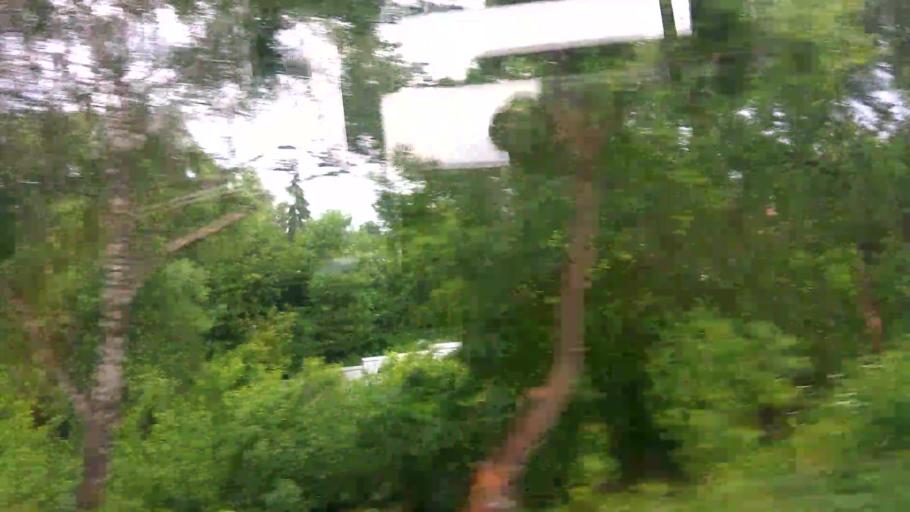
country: RU
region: Moskovskaya
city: Zaraysk
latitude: 54.7550
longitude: 38.8675
